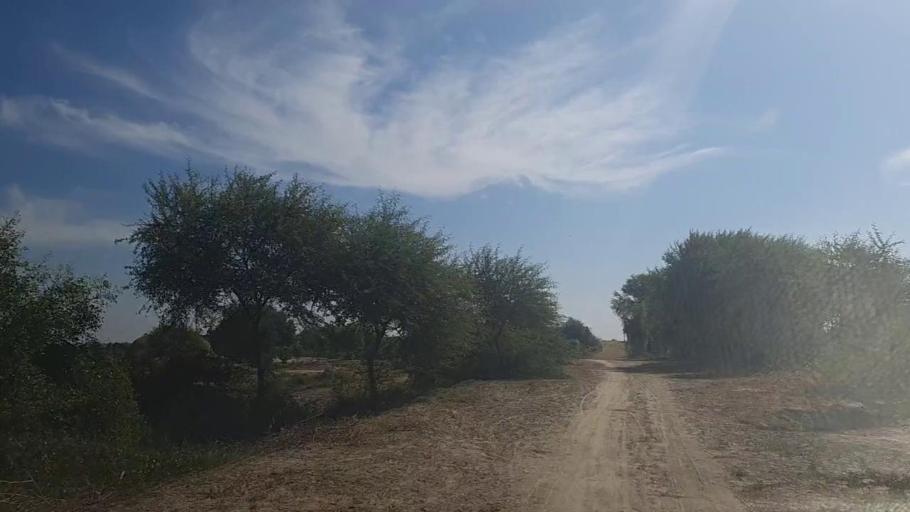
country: PK
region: Sindh
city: Mirpur Batoro
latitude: 24.6542
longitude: 68.2022
